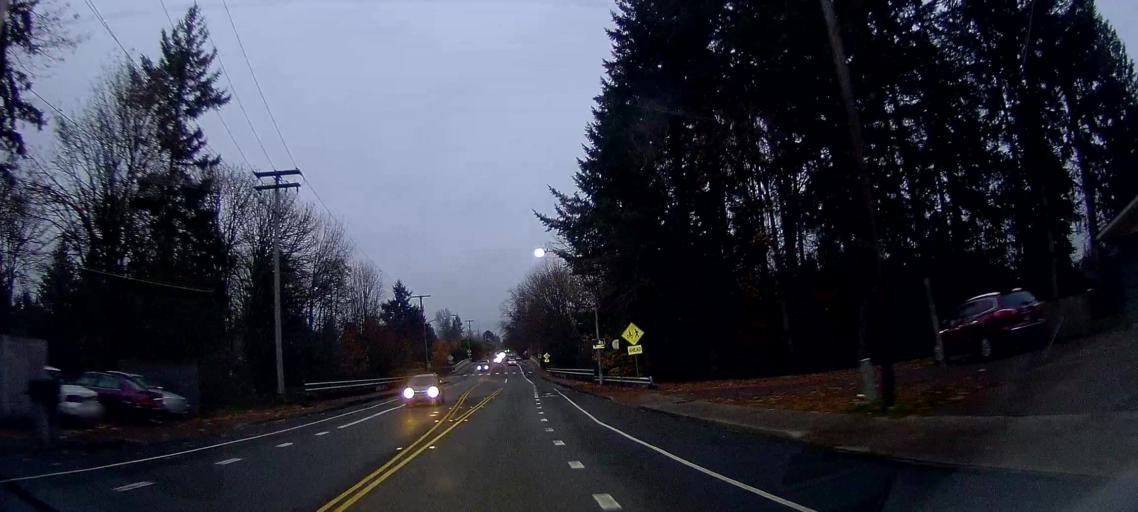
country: US
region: Washington
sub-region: Thurston County
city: Olympia
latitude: 47.0389
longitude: -122.8691
